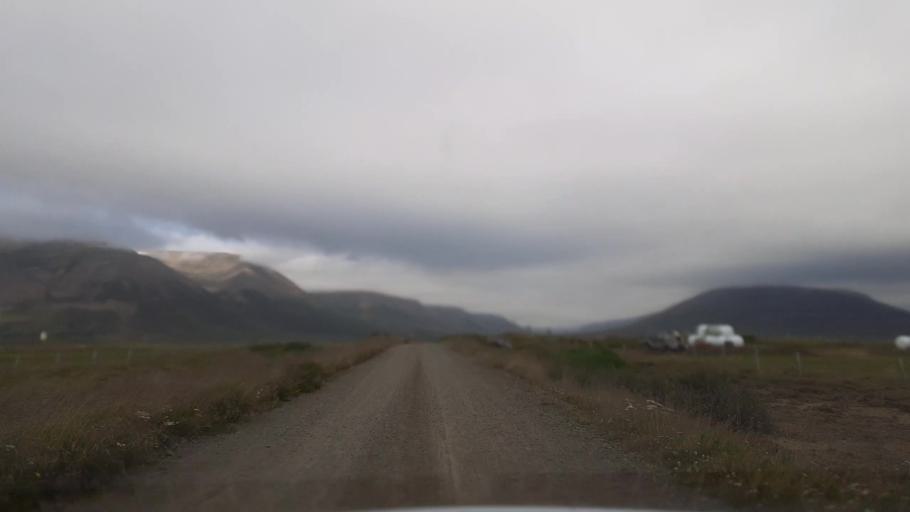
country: IS
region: Northwest
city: Saudarkrokur
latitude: 65.9027
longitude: -19.4156
